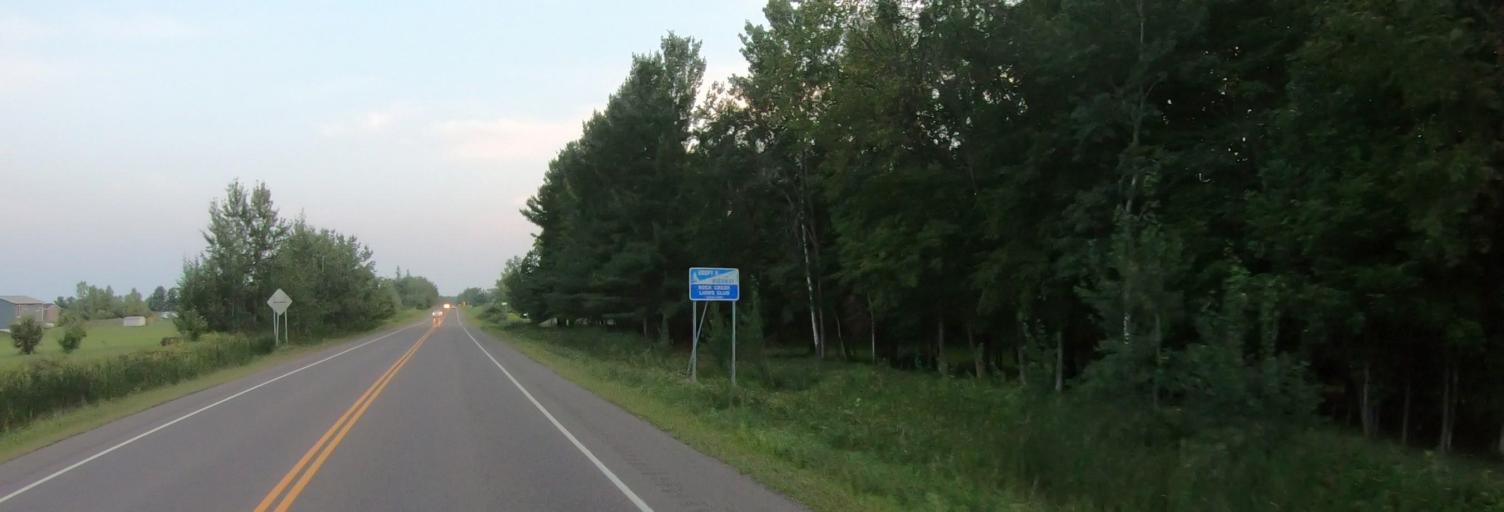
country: US
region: Minnesota
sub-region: Pine County
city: Rock Creek
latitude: 45.7723
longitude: -92.9603
